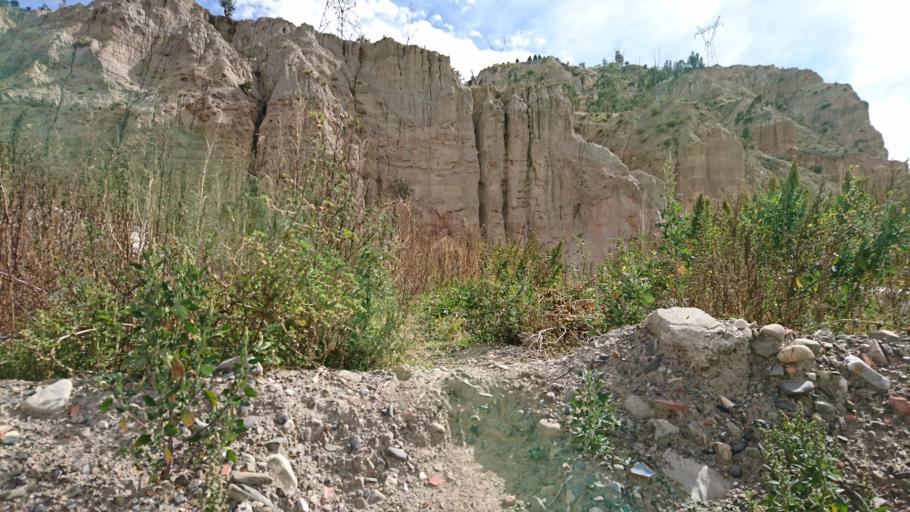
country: BO
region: La Paz
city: La Paz
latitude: -16.5306
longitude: -68.0886
